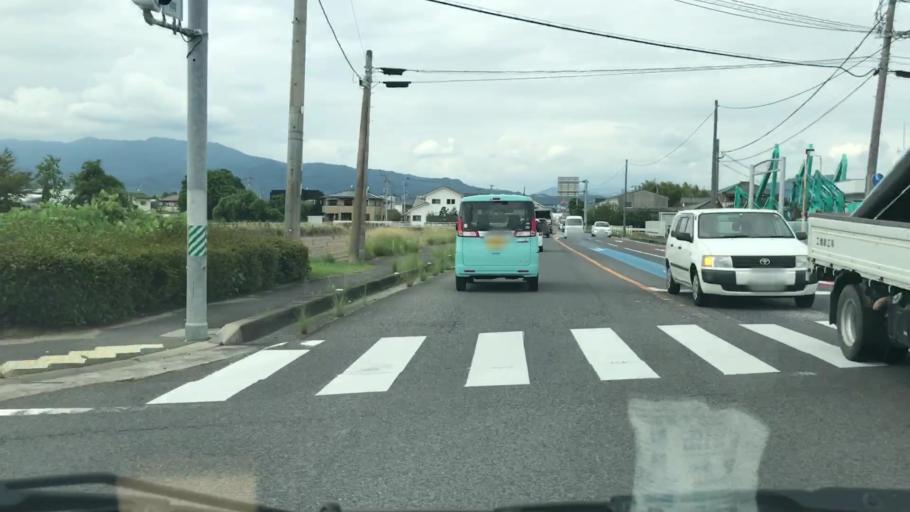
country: JP
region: Saga Prefecture
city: Saga-shi
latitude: 33.2691
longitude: 130.2616
